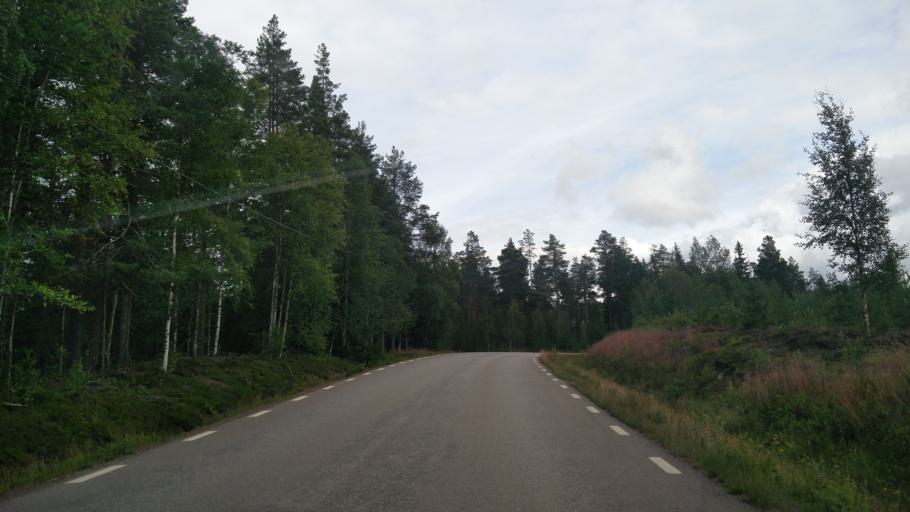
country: NO
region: Hedmark
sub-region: Trysil
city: Innbygda
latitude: 61.1766
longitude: 12.8518
